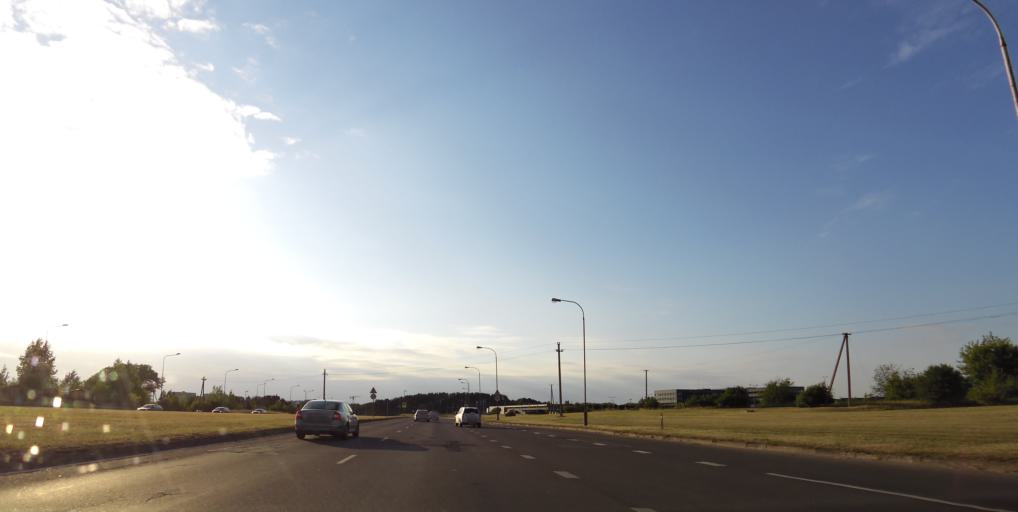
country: LT
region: Vilnius County
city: Pilaite
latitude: 54.7030
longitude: 25.2027
